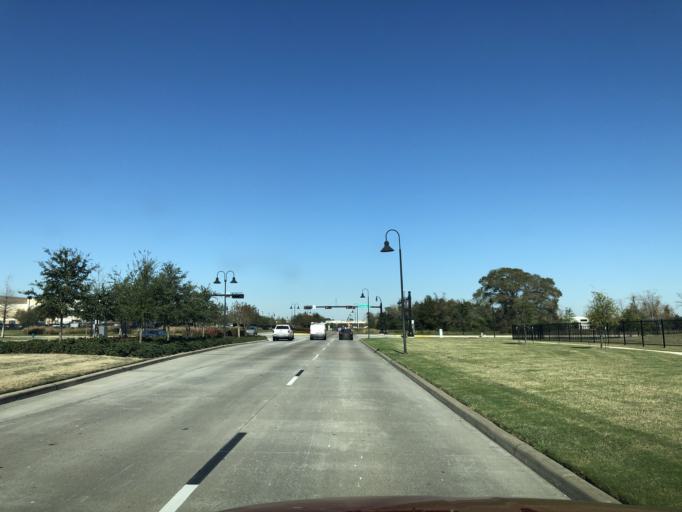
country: US
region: Texas
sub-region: Fort Bend County
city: Fresno
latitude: 29.5911
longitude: -95.4006
